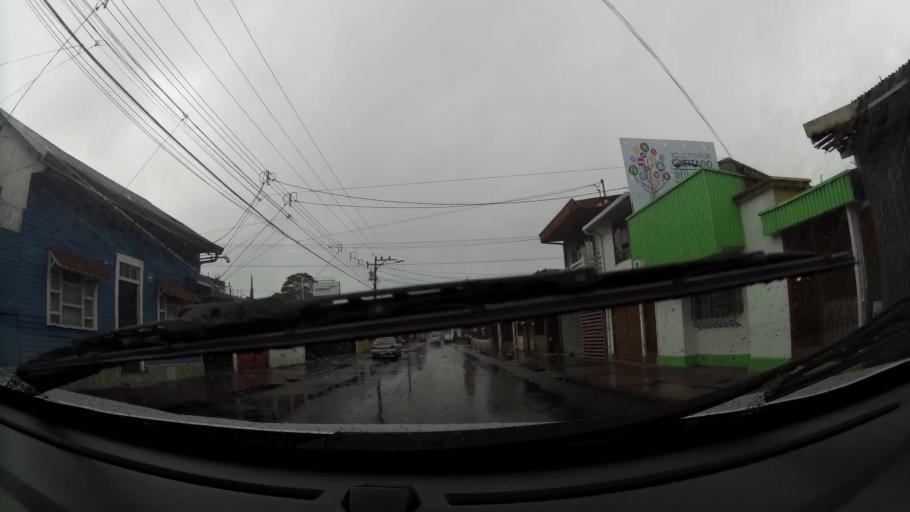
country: CR
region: Cartago
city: Cartago
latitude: 9.8658
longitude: -83.9281
